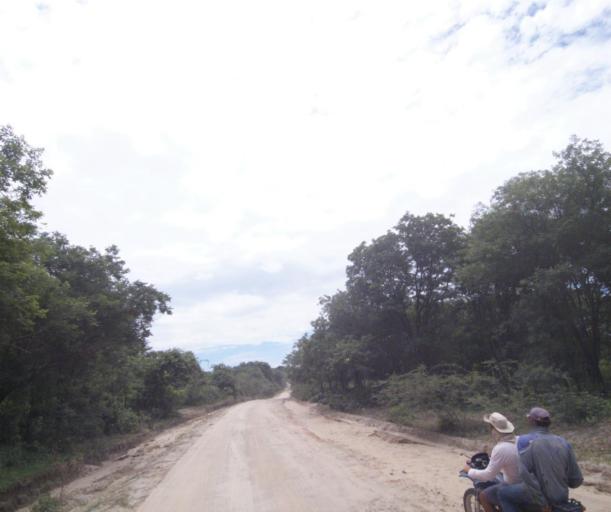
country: BR
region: Bahia
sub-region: Carinhanha
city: Carinhanha
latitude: -14.2119
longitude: -43.8991
